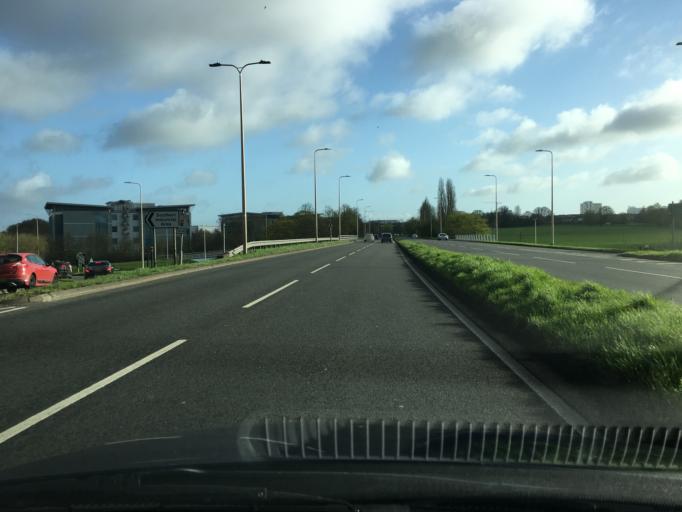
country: GB
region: England
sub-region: Bracknell Forest
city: Bracknell
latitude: 51.4069
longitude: -0.7689
